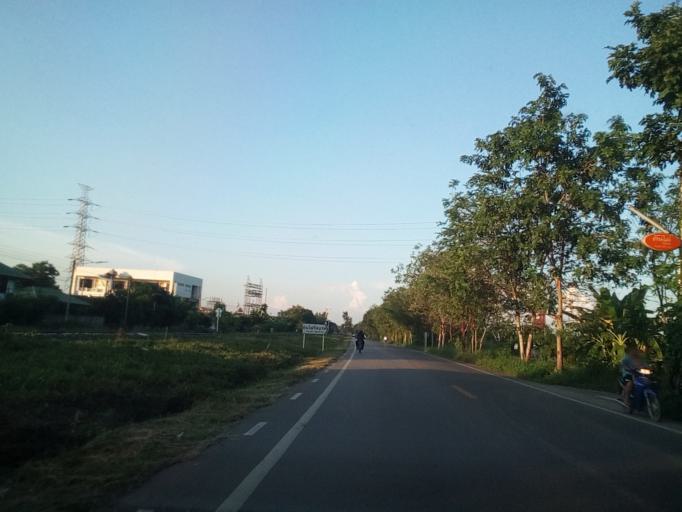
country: TH
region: Lamphun
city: Lamphun
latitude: 18.6304
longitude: 99.0403
